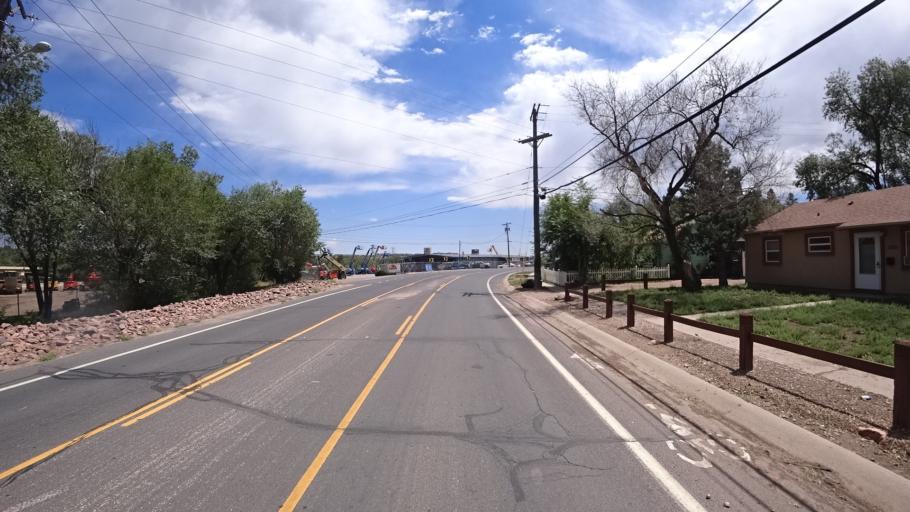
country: US
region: Colorado
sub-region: El Paso County
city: Colorado Springs
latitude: 38.8067
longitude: -104.8065
